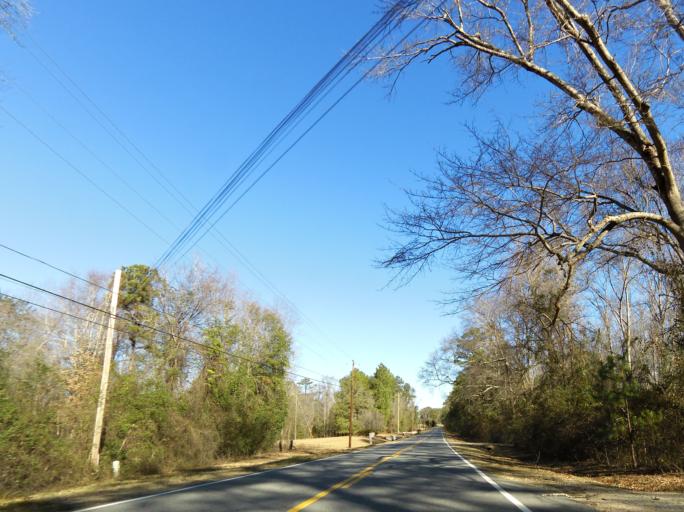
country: US
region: Georgia
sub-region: Bibb County
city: West Point
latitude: 32.7816
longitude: -83.7564
